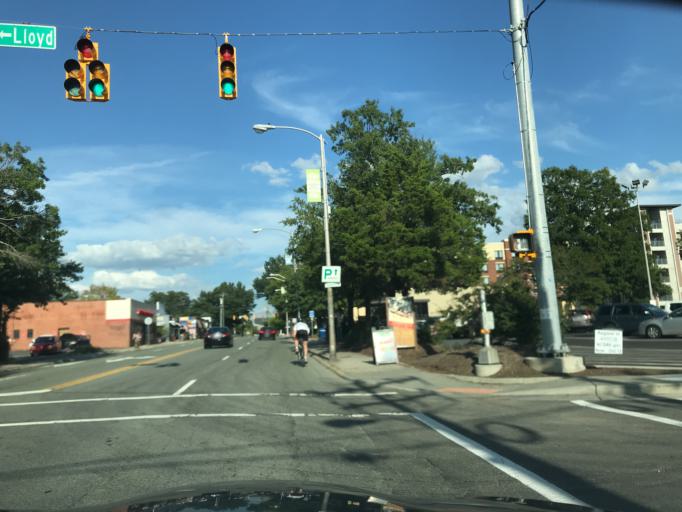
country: US
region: North Carolina
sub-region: Orange County
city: Carrboro
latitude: 35.9107
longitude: -79.0691
